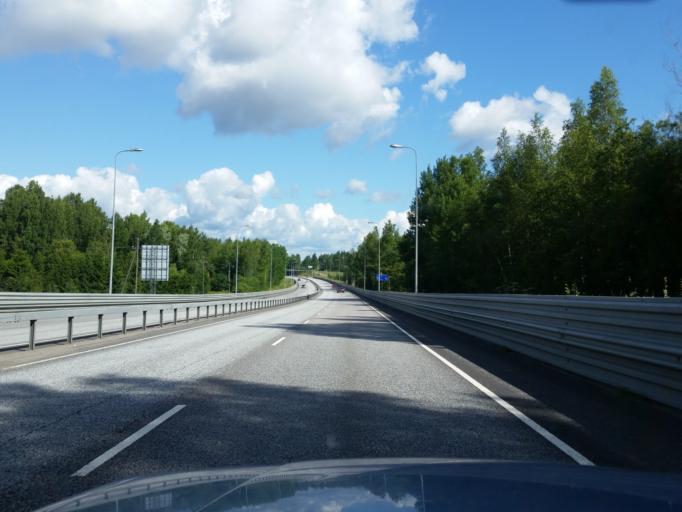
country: FI
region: Uusimaa
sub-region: Helsinki
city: Vihti
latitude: 60.3088
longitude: 24.3500
